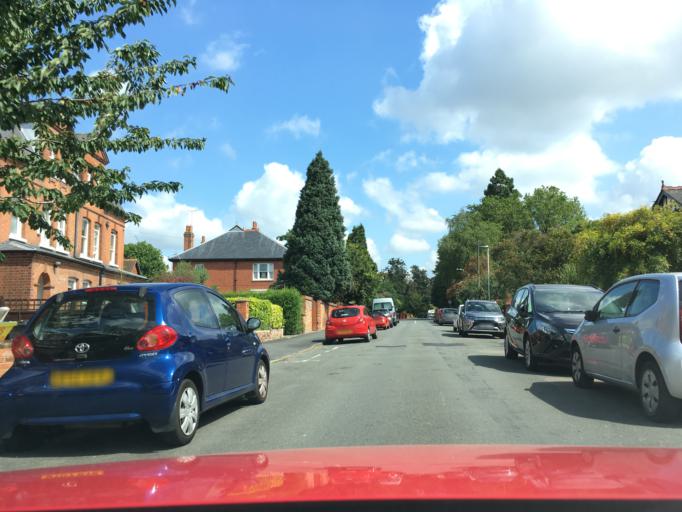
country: GB
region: England
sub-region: Gloucestershire
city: Gloucester
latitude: 51.8705
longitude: -2.2342
